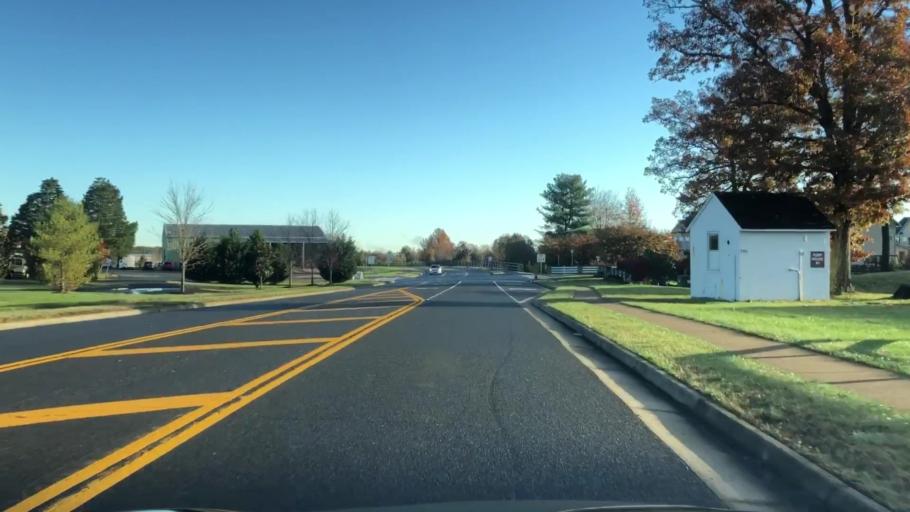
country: US
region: Virginia
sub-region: Fauquier County
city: New Baltimore
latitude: 38.7425
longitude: -77.6757
